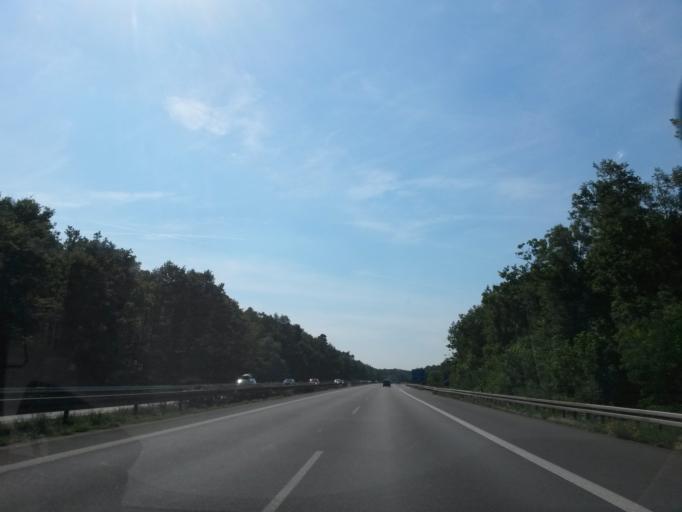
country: DE
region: Bavaria
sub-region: Regierungsbezirk Unterfranken
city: Grosslangheim
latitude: 49.7807
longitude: 10.2235
